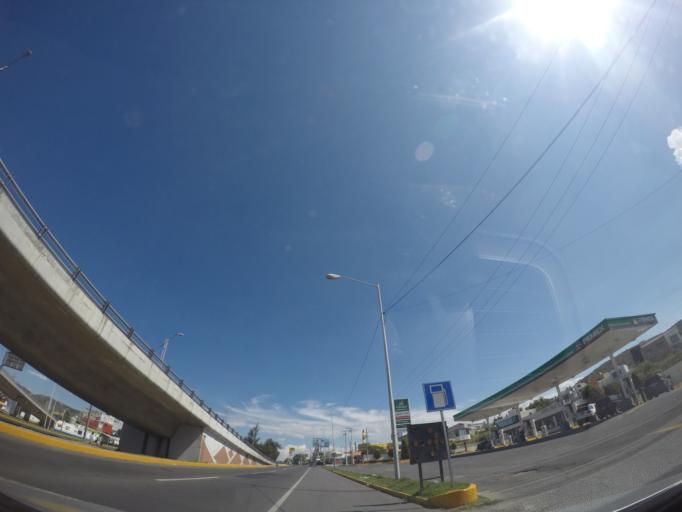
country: MX
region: Hidalgo
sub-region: Mineral de la Reforma
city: Unidad Minera 11 de Julio
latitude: 20.1023
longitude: -98.7189
